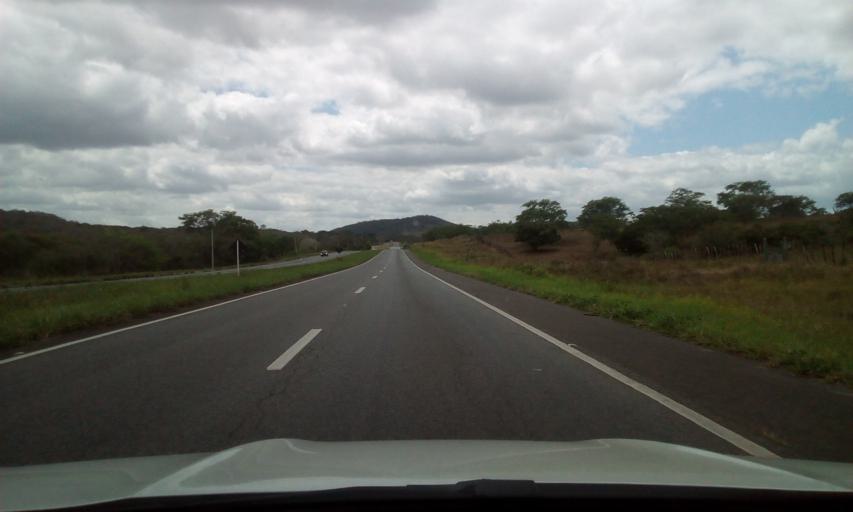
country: BR
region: Paraiba
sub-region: Fagundes
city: Fagundes
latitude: -7.2774
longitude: -35.7441
